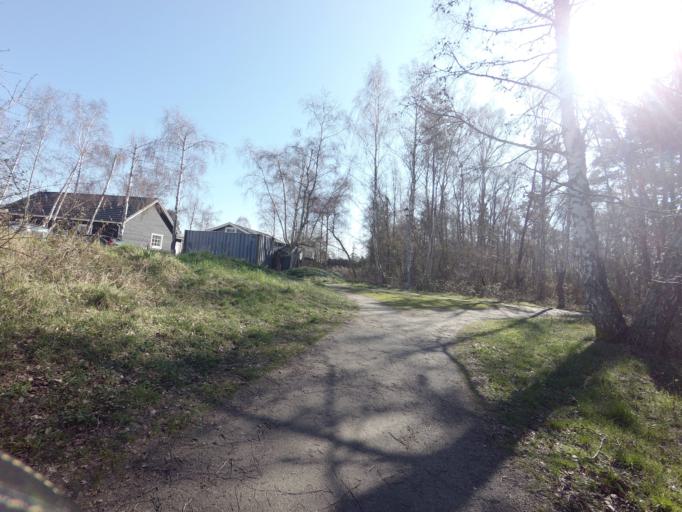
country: SE
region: Skane
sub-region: Vellinge Kommun
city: Skanor med Falsterbo
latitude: 55.4083
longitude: 12.8524
